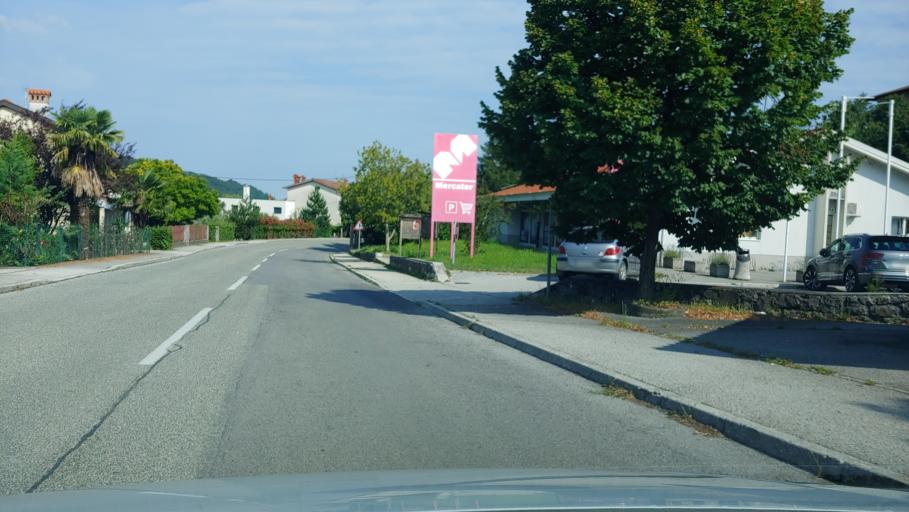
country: SI
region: Komen
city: Komen
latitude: 45.8608
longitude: 13.7858
